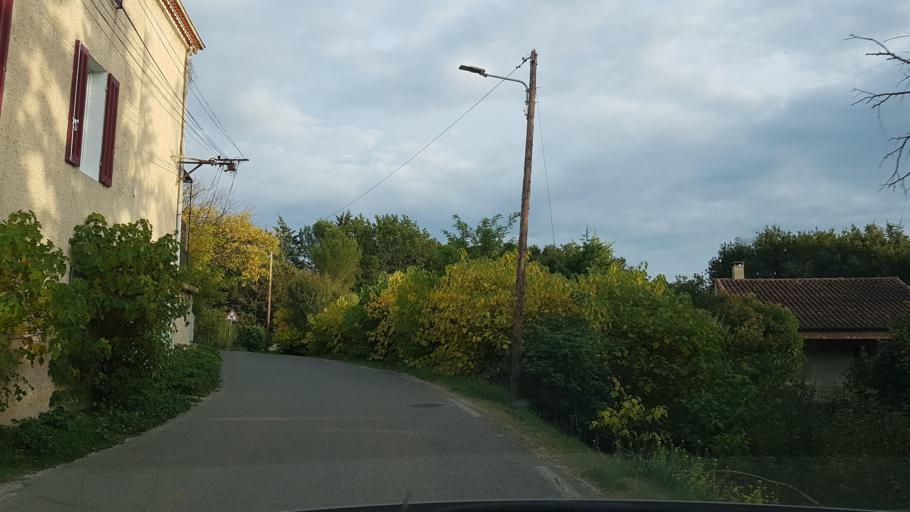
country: FR
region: Provence-Alpes-Cote d'Azur
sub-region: Departement des Bouches-du-Rhone
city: Cabries
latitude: 43.4398
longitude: 5.3778
